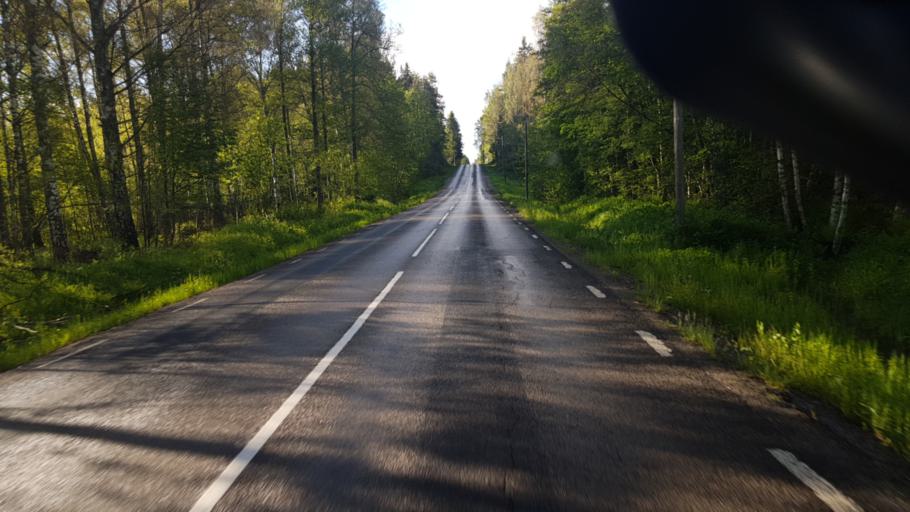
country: SE
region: Vaermland
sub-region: Arvika Kommun
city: Arvika
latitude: 59.6282
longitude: 12.4970
